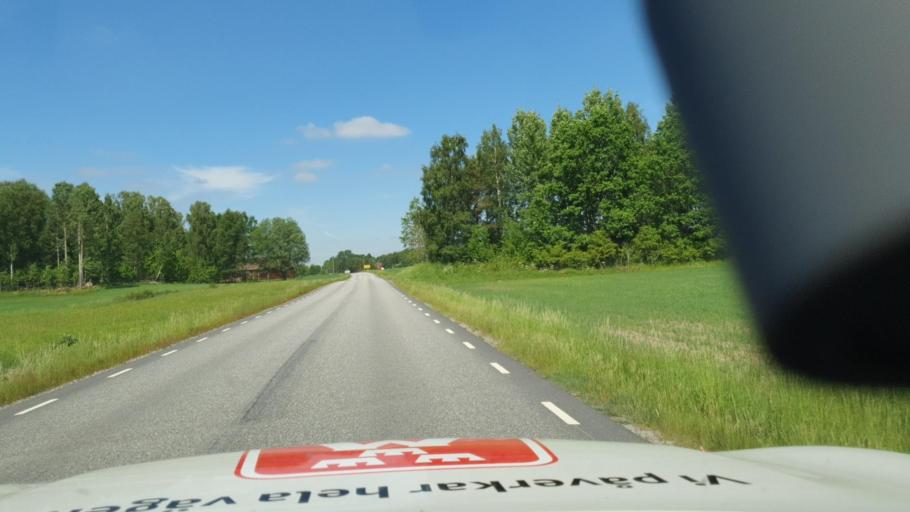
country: SE
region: Vaestra Goetaland
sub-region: Herrljunga Kommun
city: Herrljunga
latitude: 58.1616
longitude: 13.0072
